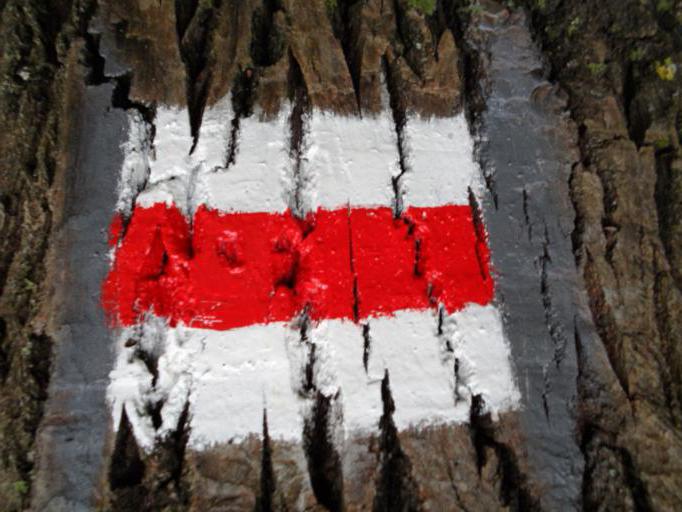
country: HU
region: Somogy
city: Marcali
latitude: 46.5537
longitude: 17.4273
